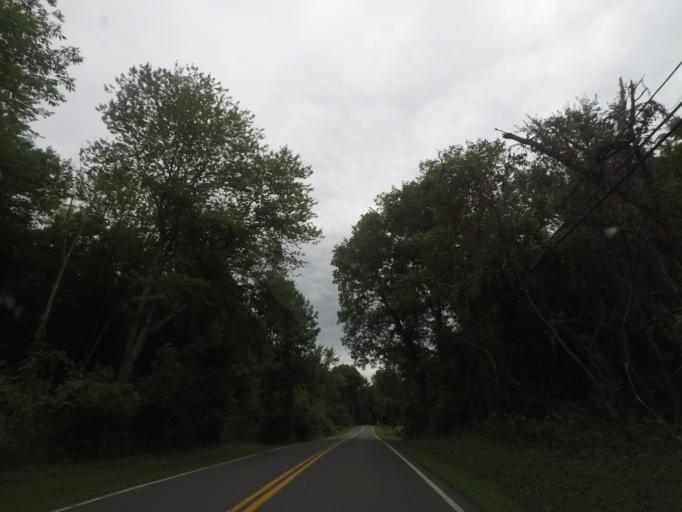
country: US
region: New York
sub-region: Rensselaer County
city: Nassau
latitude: 42.4804
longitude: -73.5925
